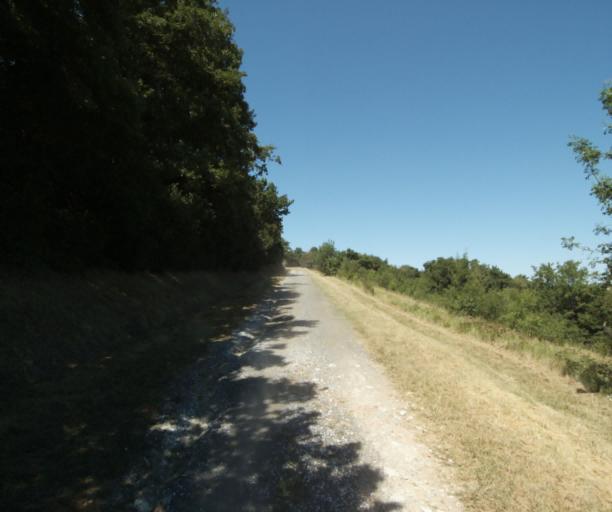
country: FR
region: Midi-Pyrenees
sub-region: Departement de la Haute-Garonne
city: Saint-Felix-Lauragais
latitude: 43.4725
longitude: 1.9189
